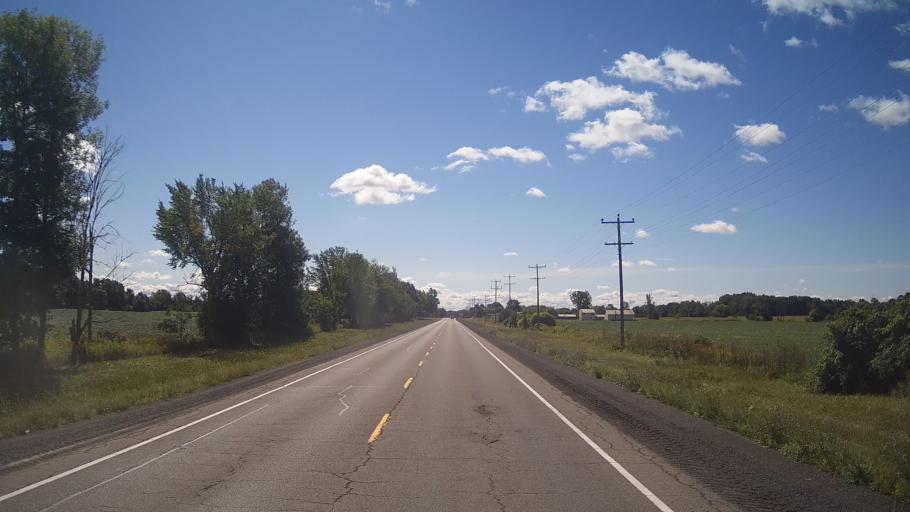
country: US
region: New York
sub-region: St. Lawrence County
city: Norfolk
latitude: 44.9446
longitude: -75.2196
